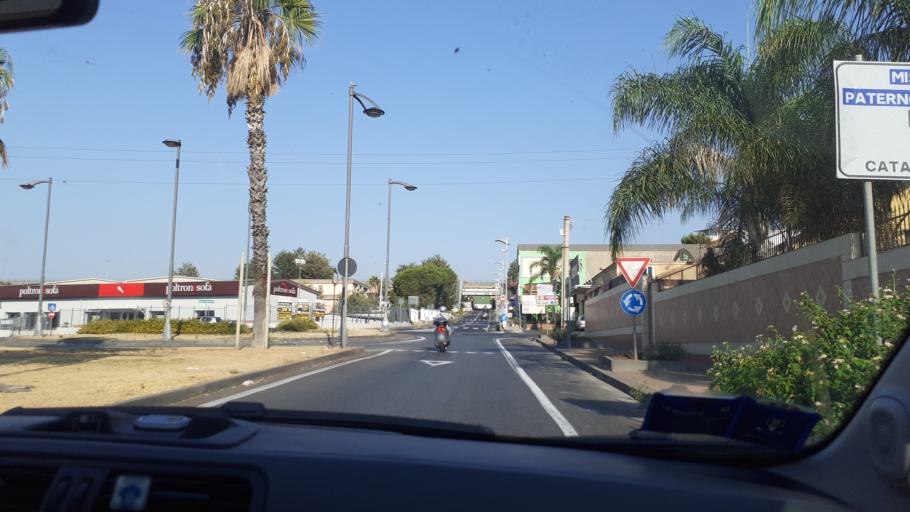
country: IT
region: Sicily
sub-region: Catania
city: Misterbianco
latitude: 37.5151
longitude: 15.0229
